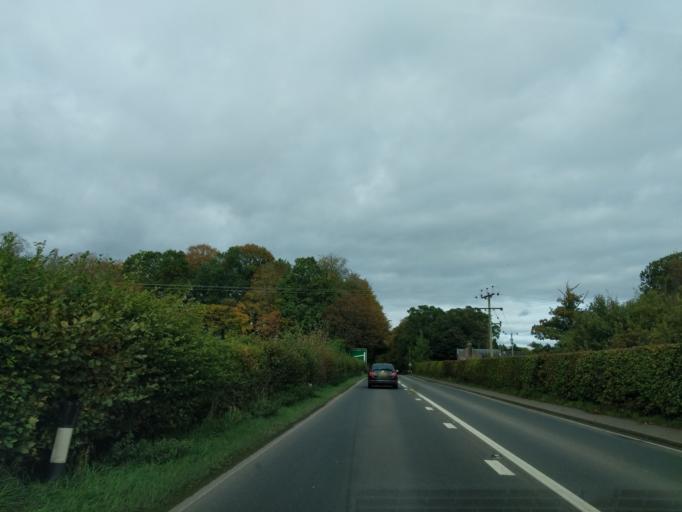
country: GB
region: Scotland
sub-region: Dumfries and Galloway
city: Thornhill
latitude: 55.2488
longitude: -3.7722
